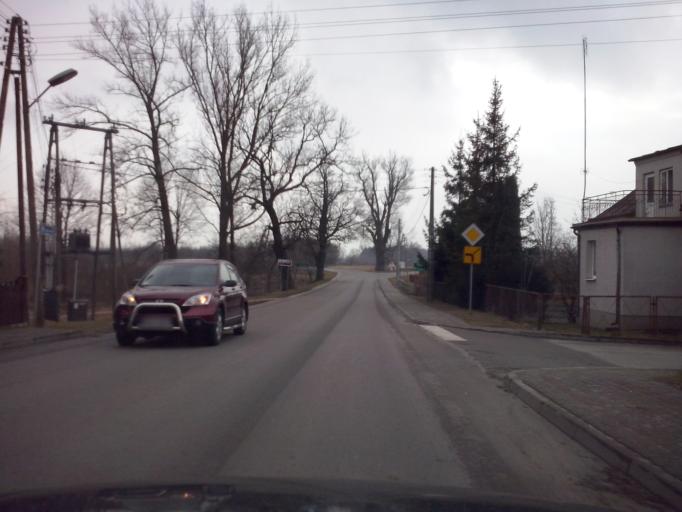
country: PL
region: Subcarpathian Voivodeship
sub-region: Powiat nizanski
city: Ulanow
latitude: 50.4884
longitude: 22.2657
